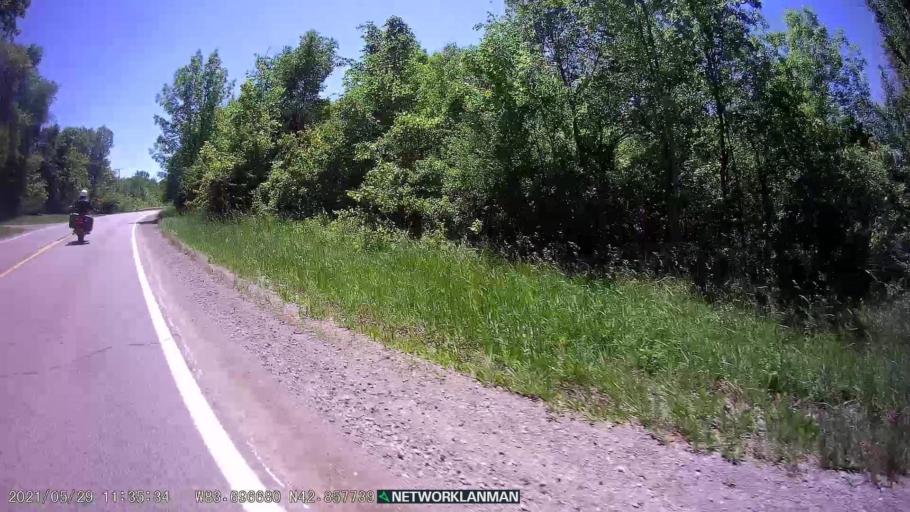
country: US
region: Michigan
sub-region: Genesee County
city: Lake Fenton
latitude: 42.8575
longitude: -83.6967
